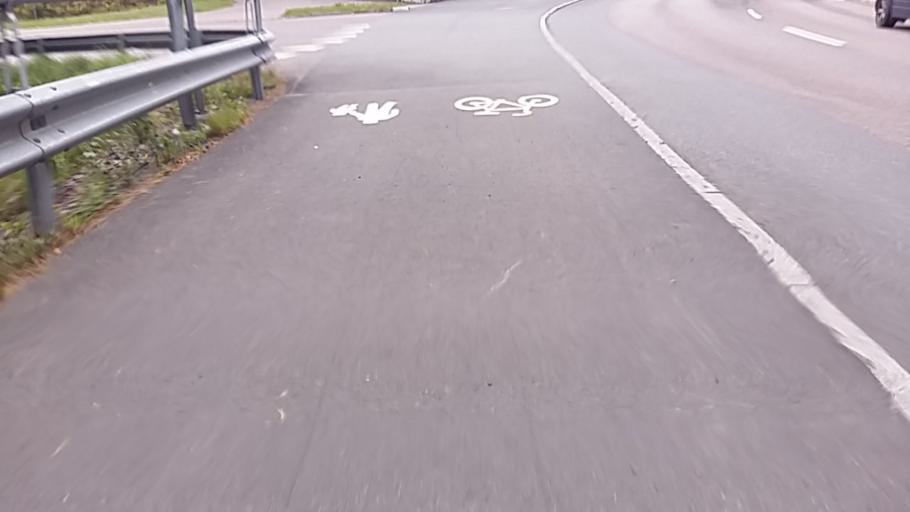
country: SE
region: Joenkoeping
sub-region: Jonkopings Kommun
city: Odensjo
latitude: 57.7149
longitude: 14.1240
